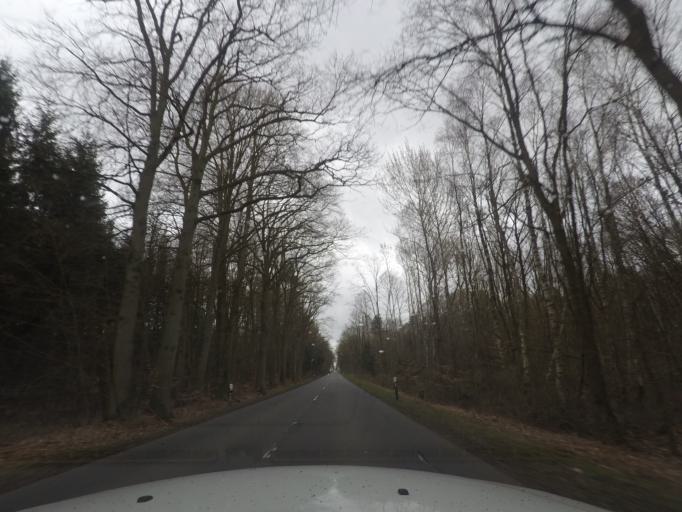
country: DE
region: Lower Saxony
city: Emmendorf
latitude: 53.0256
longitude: 10.6042
